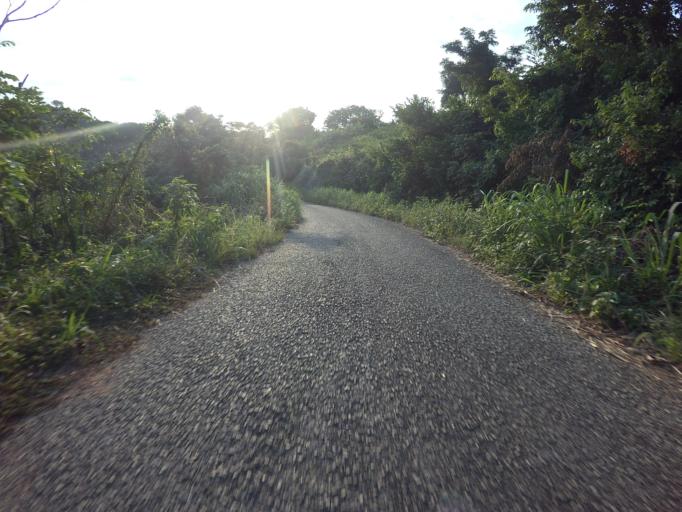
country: TG
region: Plateaux
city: Kpalime
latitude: 6.8856
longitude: 0.4459
